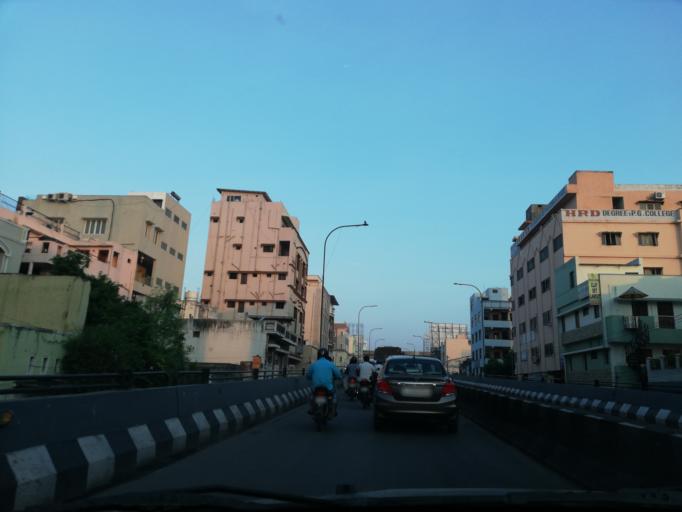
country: IN
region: Telangana
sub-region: Hyderabad
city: Hyderabad
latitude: 17.3970
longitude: 78.4955
